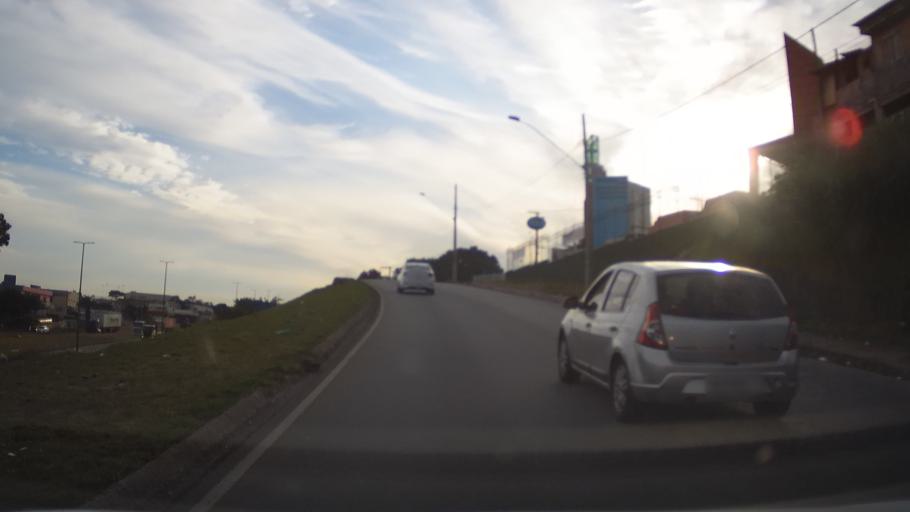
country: BR
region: Minas Gerais
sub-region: Belo Horizonte
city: Belo Horizonte
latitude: -19.8837
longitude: -43.9631
